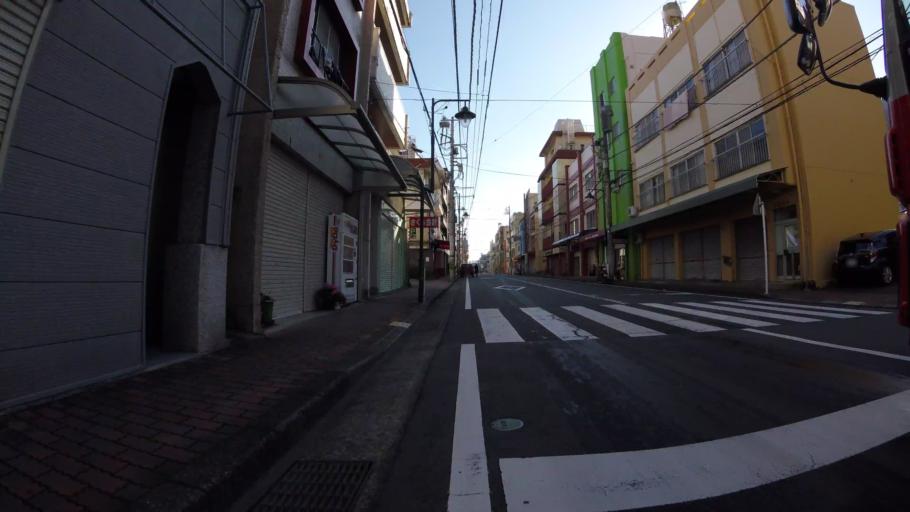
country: JP
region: Shizuoka
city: Atami
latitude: 35.0908
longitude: 139.0711
